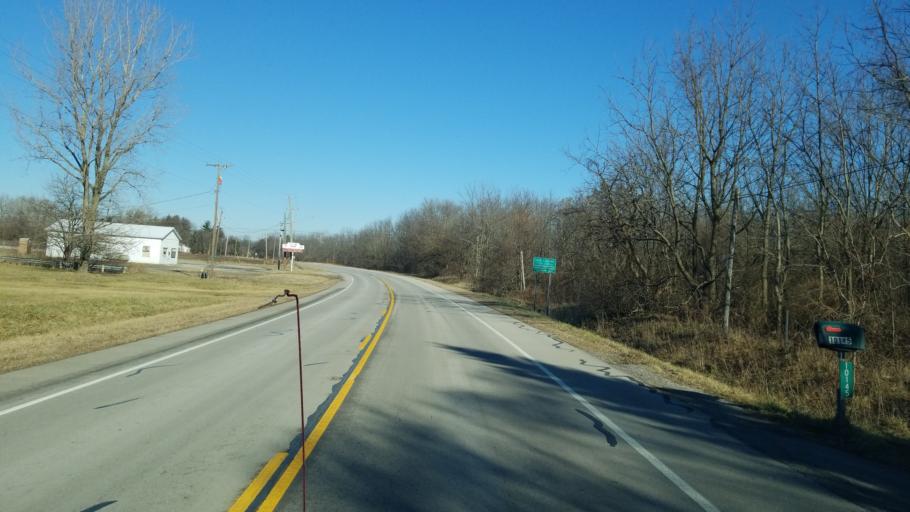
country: US
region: Ohio
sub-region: Lucas County
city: Whitehouse
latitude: 41.4564
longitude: -83.7843
